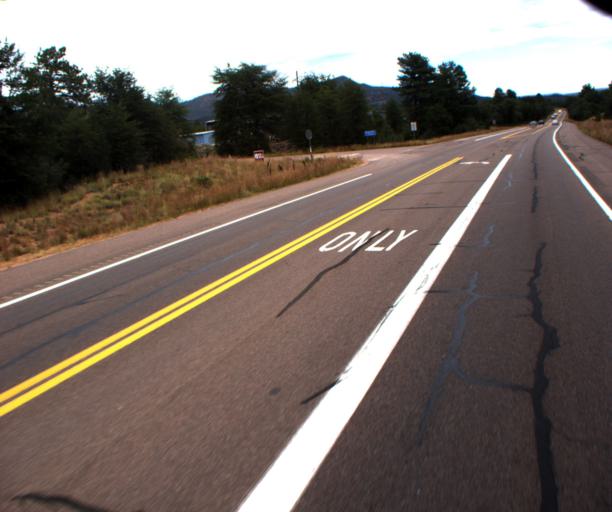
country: US
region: Arizona
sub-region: Gila County
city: Star Valley
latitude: 34.2635
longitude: -111.2412
